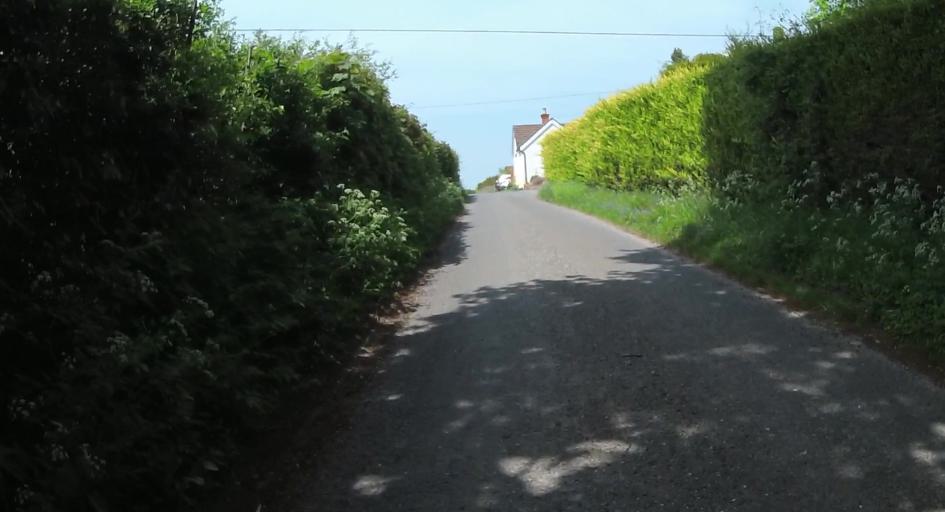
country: GB
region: England
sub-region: Hampshire
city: Overton
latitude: 51.2617
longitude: -1.2321
